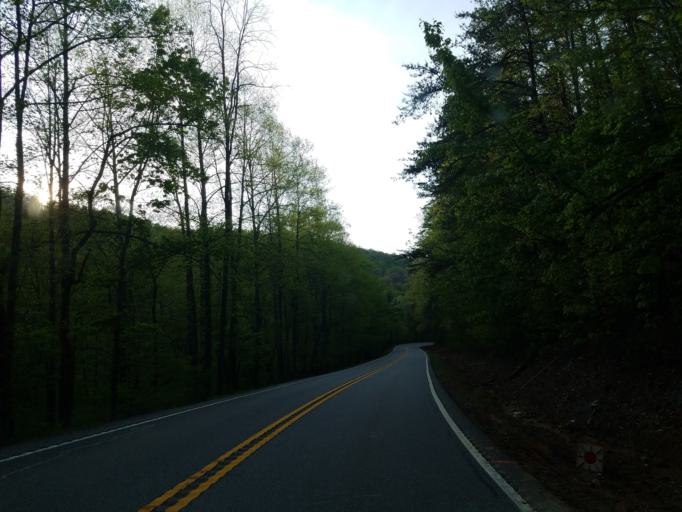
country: US
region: Georgia
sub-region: Fannin County
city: Blue Ridge
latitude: 34.8136
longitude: -84.1865
